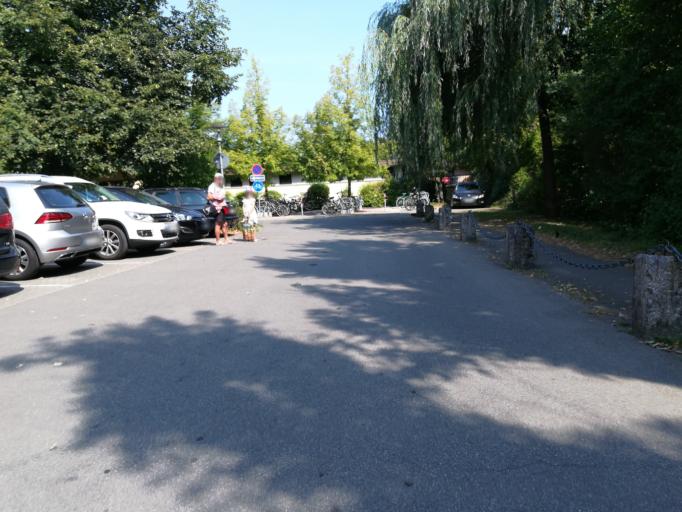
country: DE
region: Baden-Wuerttemberg
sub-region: Freiburg Region
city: Singen
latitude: 47.7625
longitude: 8.8291
